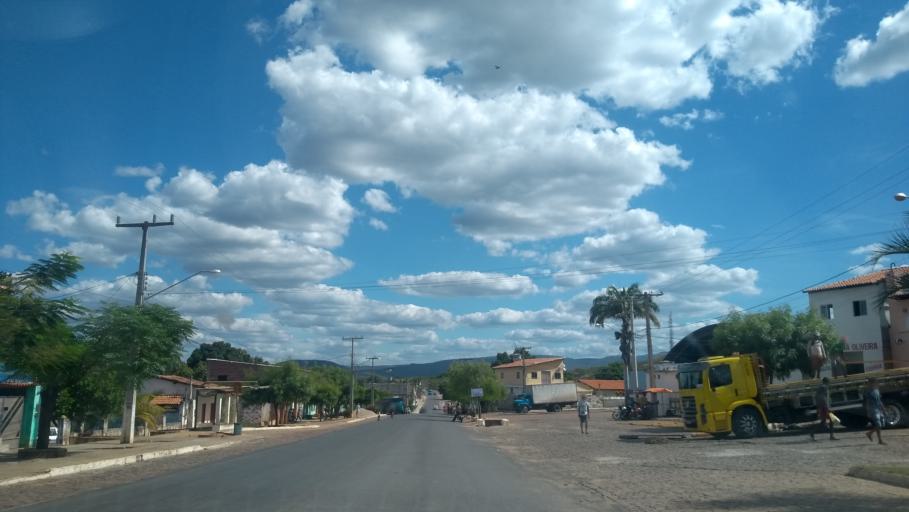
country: BR
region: Bahia
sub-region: Andarai
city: Vera Cruz
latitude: -12.7965
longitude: -41.3276
